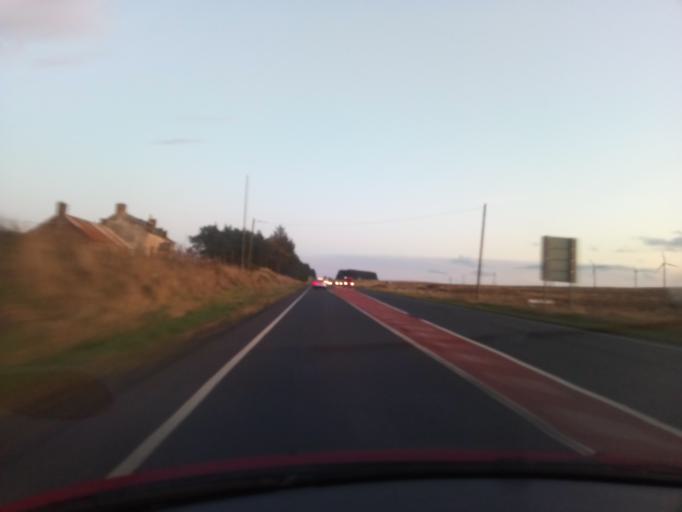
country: GB
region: Scotland
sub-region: East Lothian
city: Pencaitland
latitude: 55.8168
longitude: -2.8463
